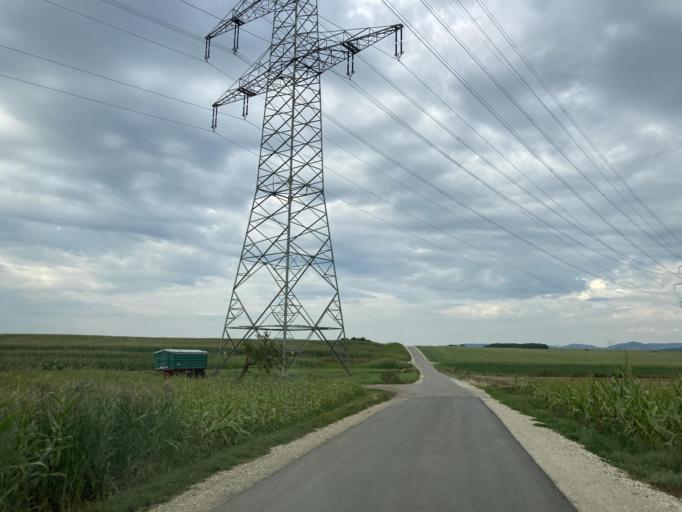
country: DE
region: Baden-Wuerttemberg
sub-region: Freiburg Region
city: Hufingen
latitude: 47.9207
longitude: 8.5447
